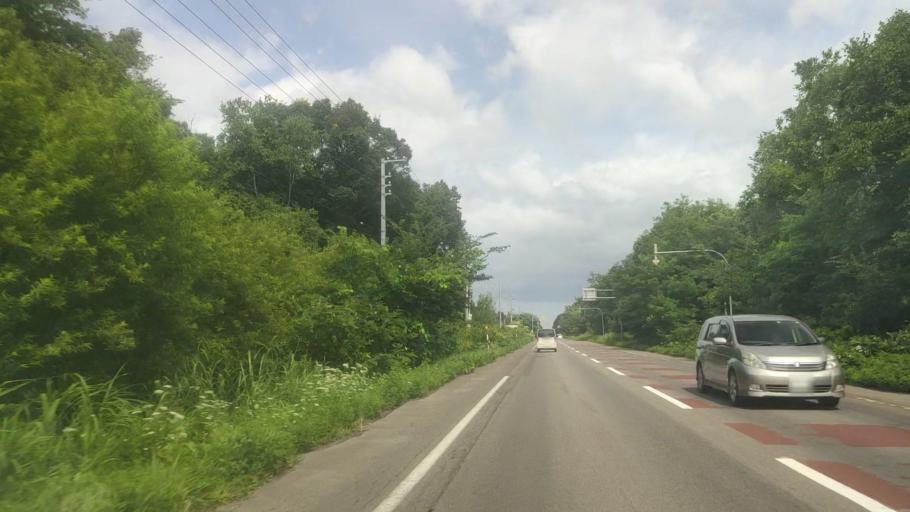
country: JP
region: Hokkaido
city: Nanae
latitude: 42.0263
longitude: 140.6121
